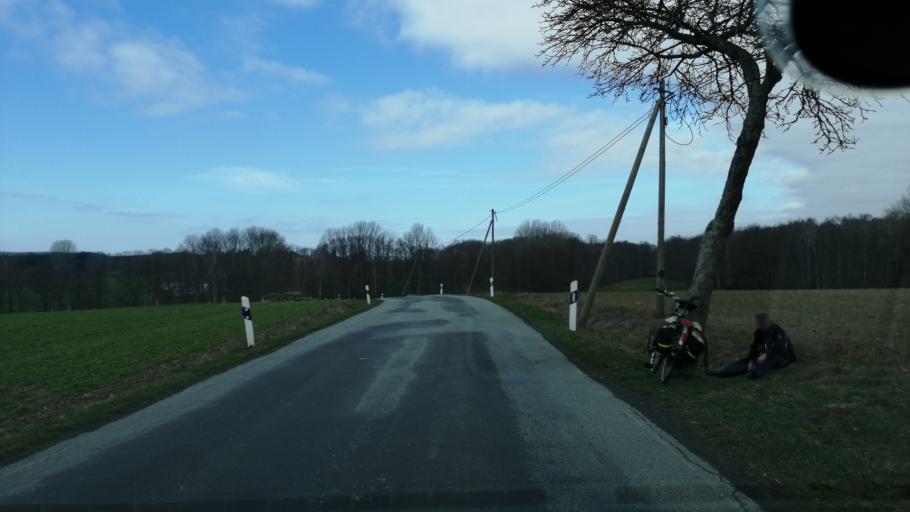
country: DE
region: Saxony
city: Herrnhut
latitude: 51.0268
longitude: 14.7107
